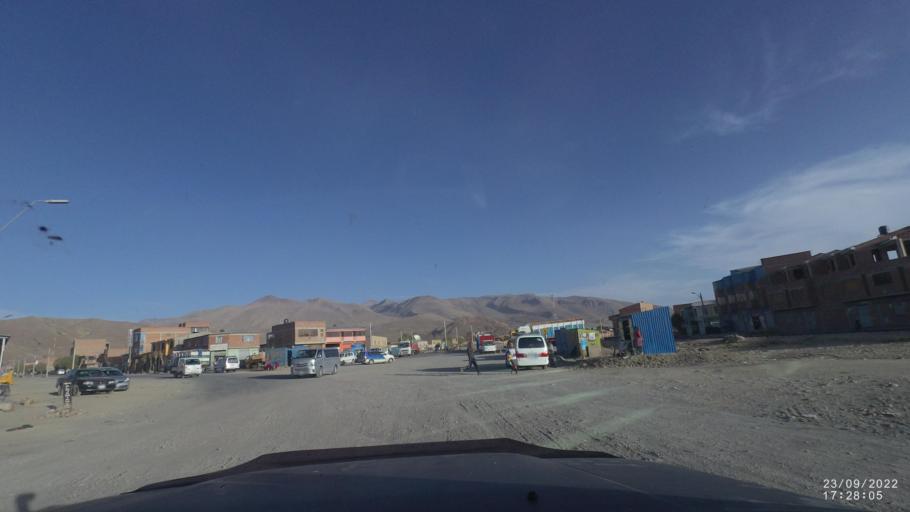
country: BO
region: Oruro
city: Challapata
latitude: -18.8944
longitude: -66.7781
